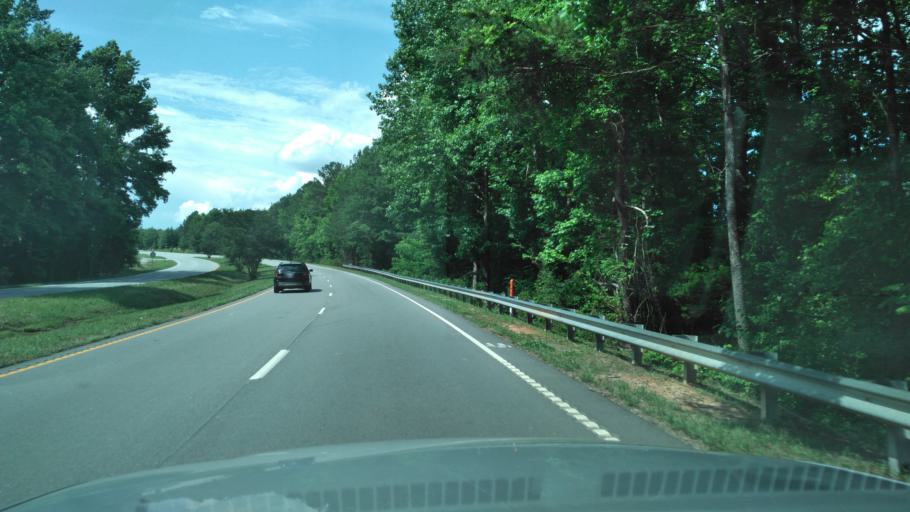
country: US
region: South Carolina
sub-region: Spartanburg County
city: Roebuck
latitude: 34.8790
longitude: -81.9564
